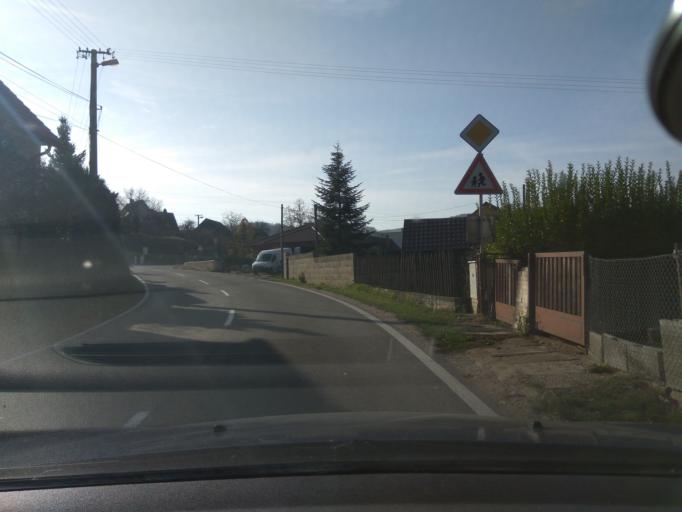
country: SK
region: Nitriansky
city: Brezova pod Bradlom
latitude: 48.6291
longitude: 17.4891
